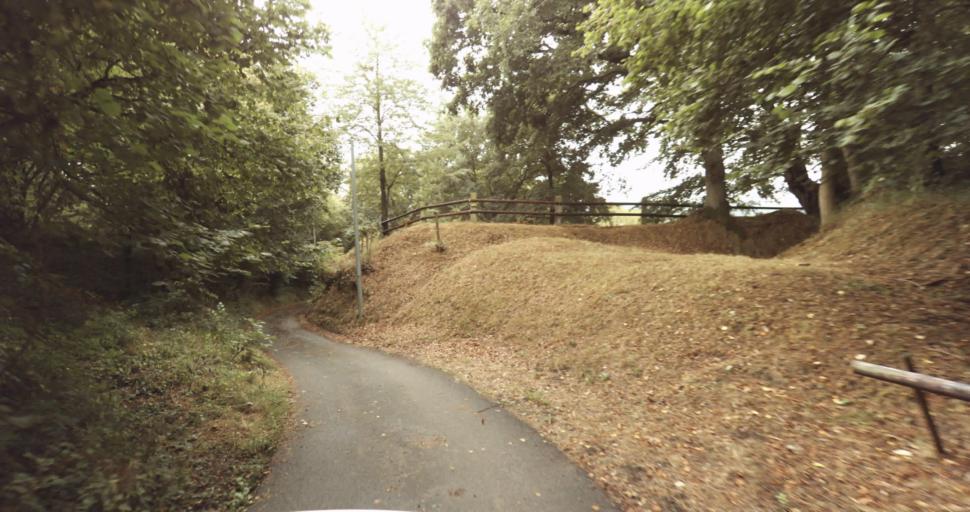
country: FR
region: Lower Normandy
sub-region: Departement du Calvados
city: Livarot
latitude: 48.9348
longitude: 0.0871
